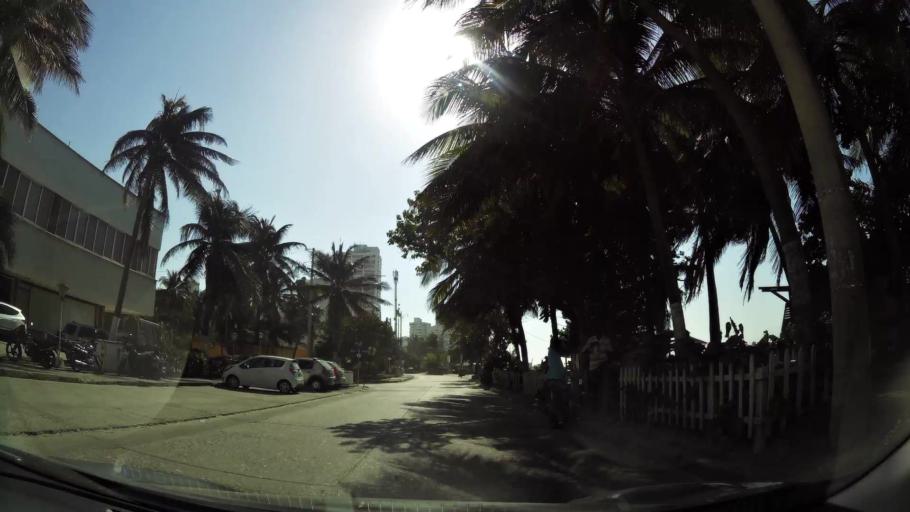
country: CO
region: Bolivar
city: Cartagena
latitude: 10.3995
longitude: -75.5605
